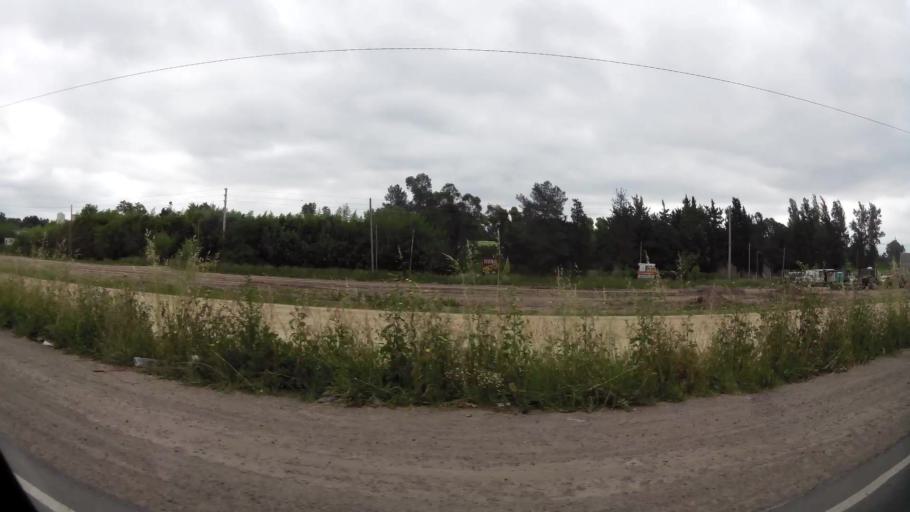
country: AR
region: Buenos Aires
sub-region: Partido de Ezeiza
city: Ezeiza
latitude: -34.8910
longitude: -58.5068
